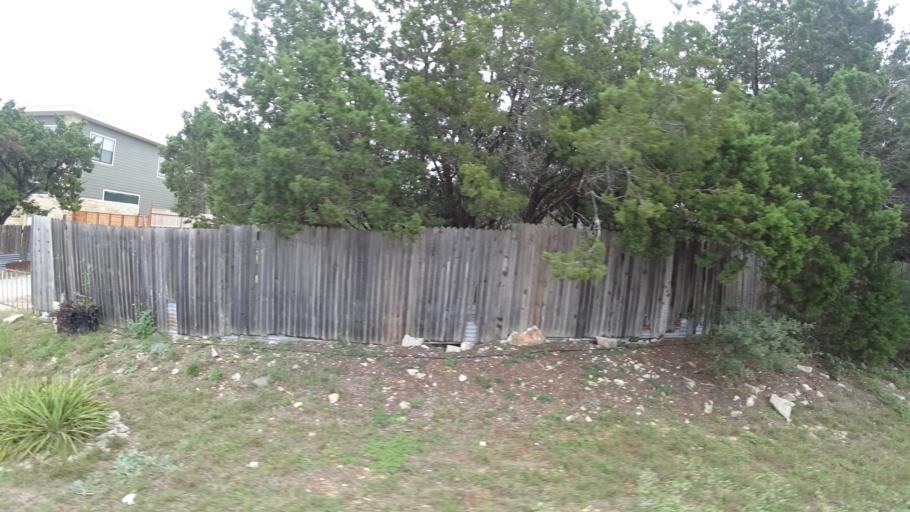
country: US
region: Texas
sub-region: Travis County
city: Hudson Bend
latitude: 30.3833
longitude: -97.9407
